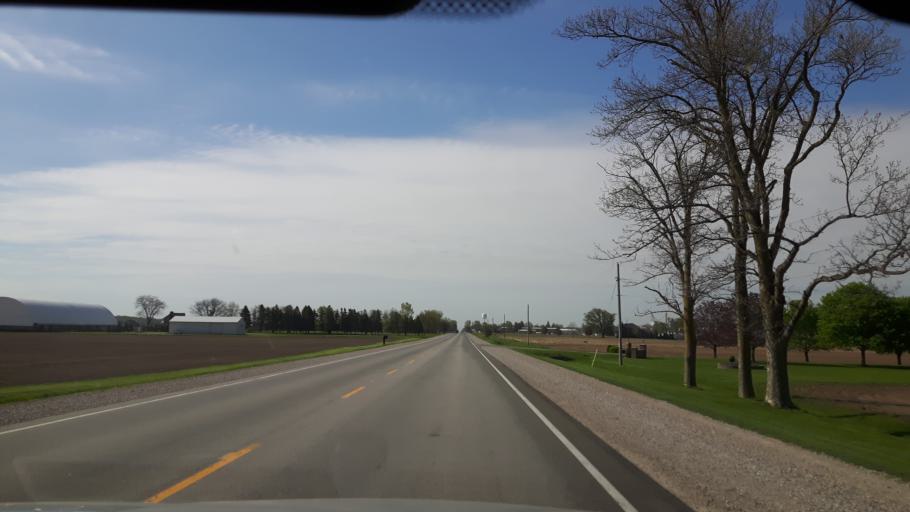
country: CA
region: Ontario
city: Bluewater
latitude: 43.4489
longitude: -81.5016
